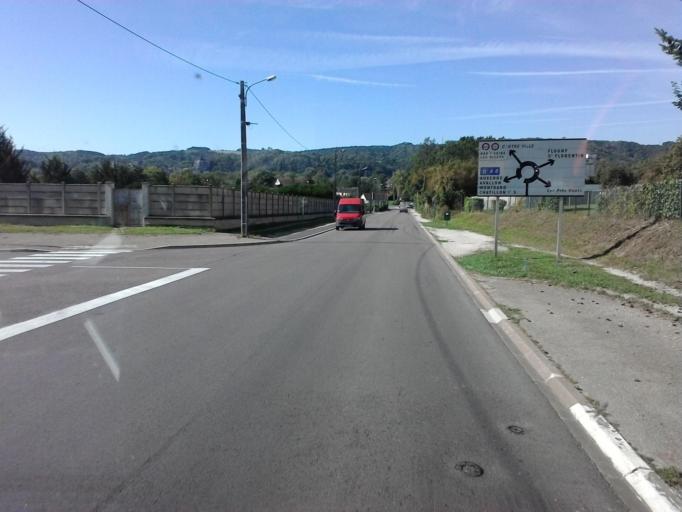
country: FR
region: Bourgogne
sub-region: Departement de l'Yonne
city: Tonnerre
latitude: 47.8640
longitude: 3.9858
